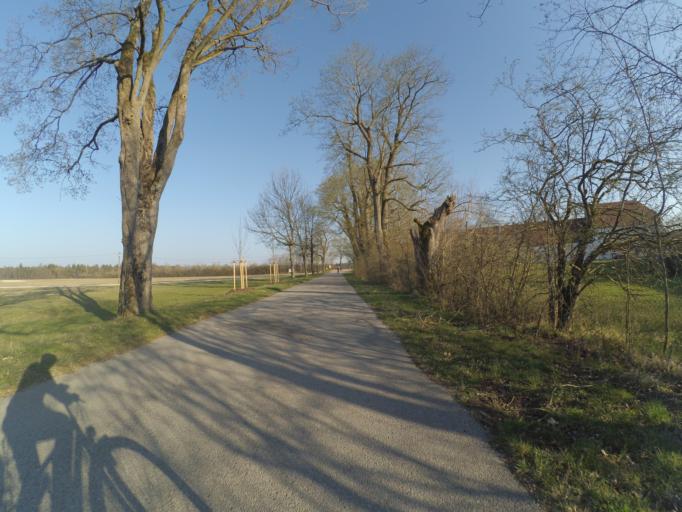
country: DE
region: Bavaria
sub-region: Upper Bavaria
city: Oberschleissheim
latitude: 48.2371
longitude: 11.5758
